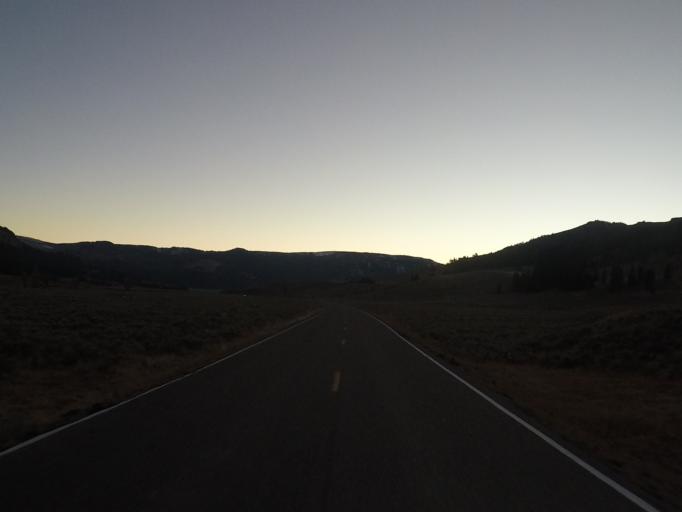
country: US
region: Montana
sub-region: Park County
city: Livingston
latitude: 44.8928
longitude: -110.1335
